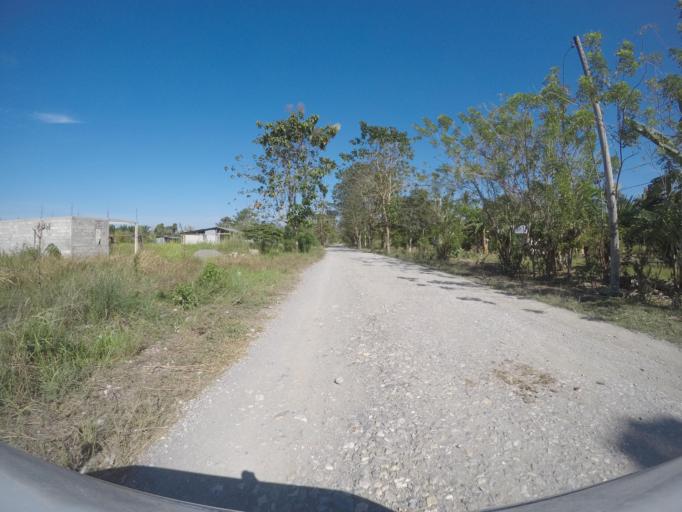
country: TL
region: Viqueque
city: Viqueque
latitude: -8.9338
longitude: 126.1317
